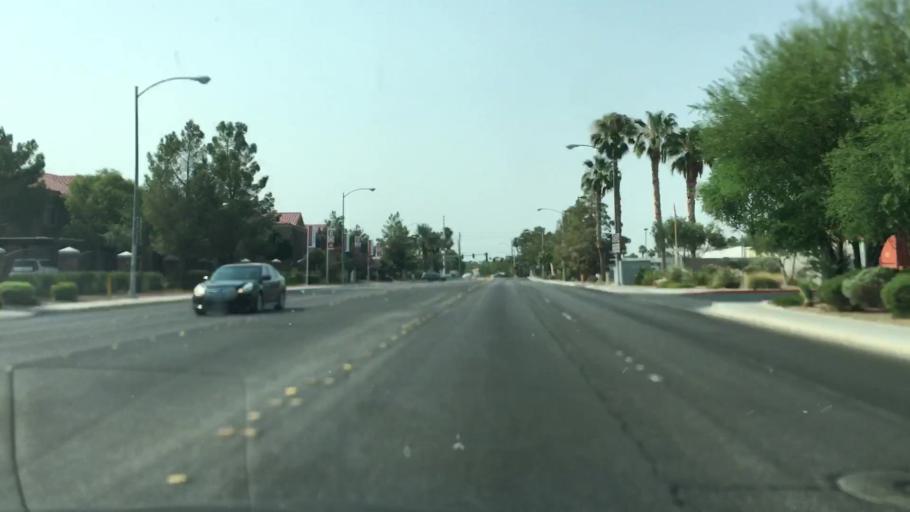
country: US
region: Nevada
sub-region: Clark County
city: Whitney
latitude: 36.0737
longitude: -115.0918
